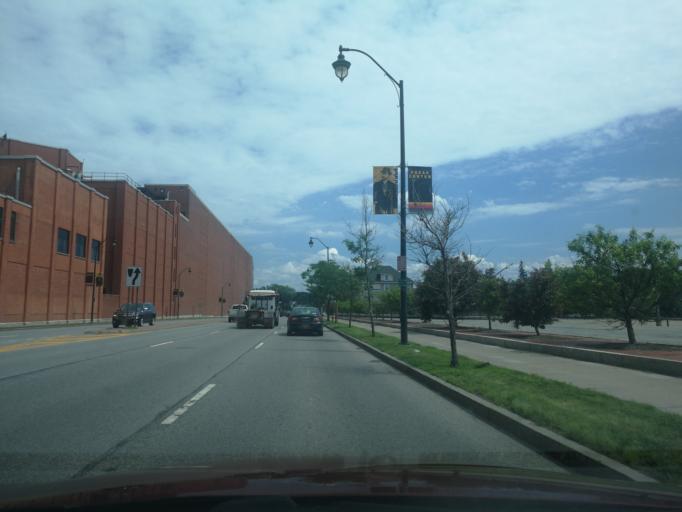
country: US
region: New York
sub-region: Monroe County
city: Rochester
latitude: 43.1966
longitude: -77.6319
